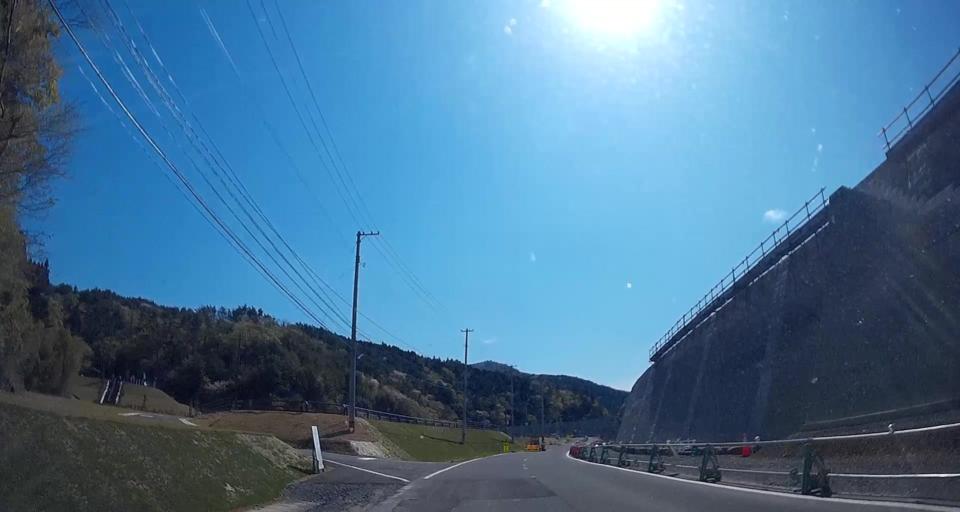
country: JP
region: Miyagi
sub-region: Oshika Gun
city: Onagawa Cho
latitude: 38.5209
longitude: 141.4737
